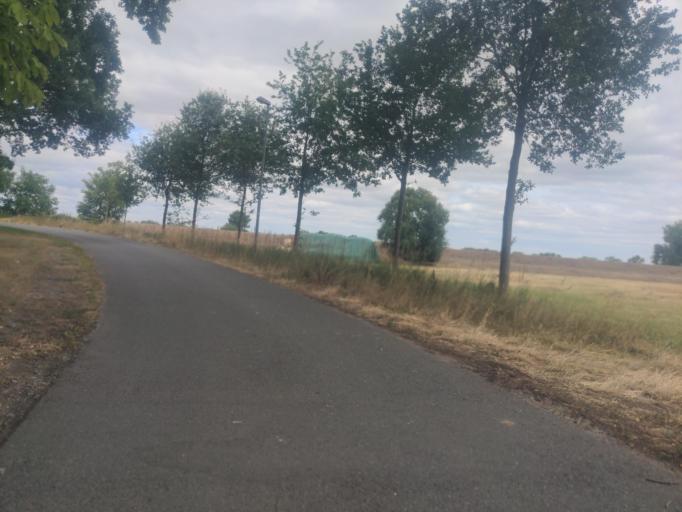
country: DE
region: Lower Saxony
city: Neu Darchau
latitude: 53.2417
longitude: 10.8538
